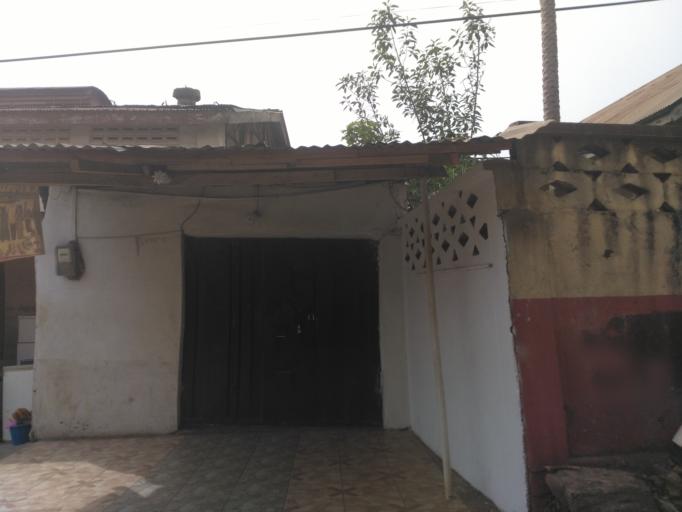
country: GH
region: Ashanti
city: Kumasi
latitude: 6.6935
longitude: -1.6185
